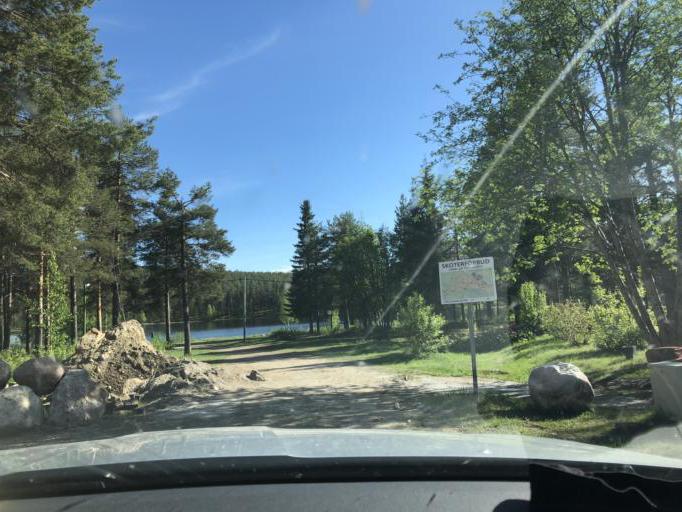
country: SE
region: Norrbotten
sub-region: Jokkmokks Kommun
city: Jokkmokk
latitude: 66.6026
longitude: 19.8284
